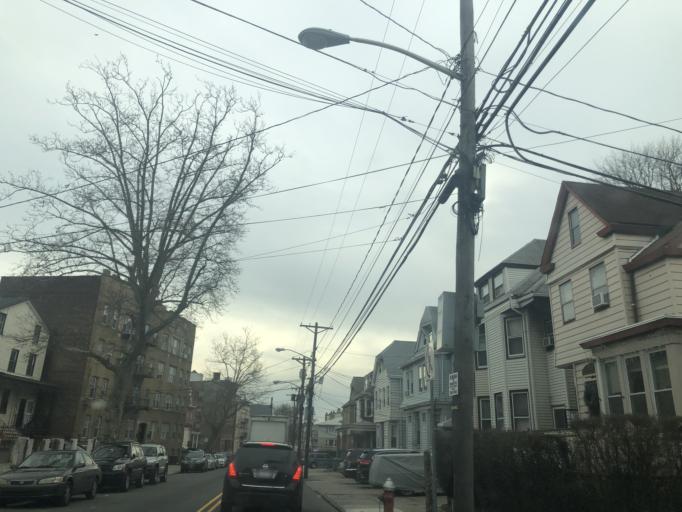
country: US
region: New Jersey
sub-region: Hudson County
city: Jersey City
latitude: 40.7215
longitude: -74.0659
